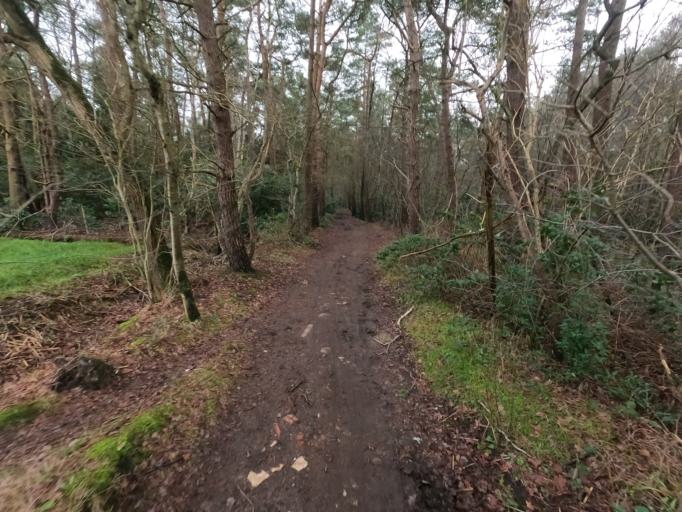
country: BE
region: Flanders
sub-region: Provincie Antwerpen
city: Brecht
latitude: 51.3000
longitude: 4.6044
